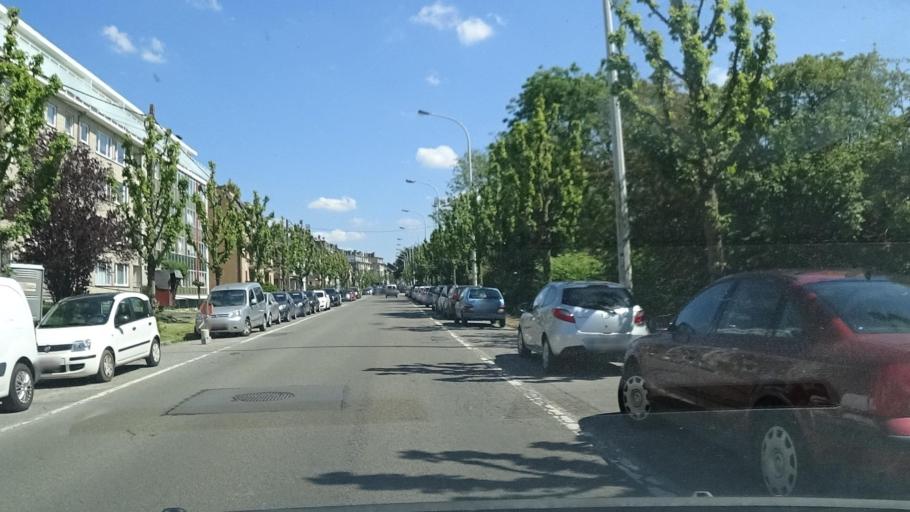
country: BE
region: Wallonia
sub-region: Province du Hainaut
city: La Louviere
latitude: 50.4765
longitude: 4.1982
